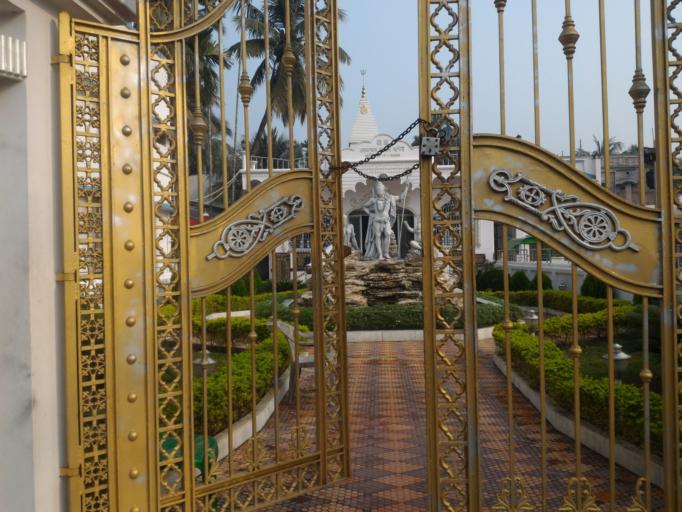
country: IN
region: West Bengal
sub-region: North 24 Parganas
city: Bangaon
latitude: 23.0366
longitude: 88.8326
